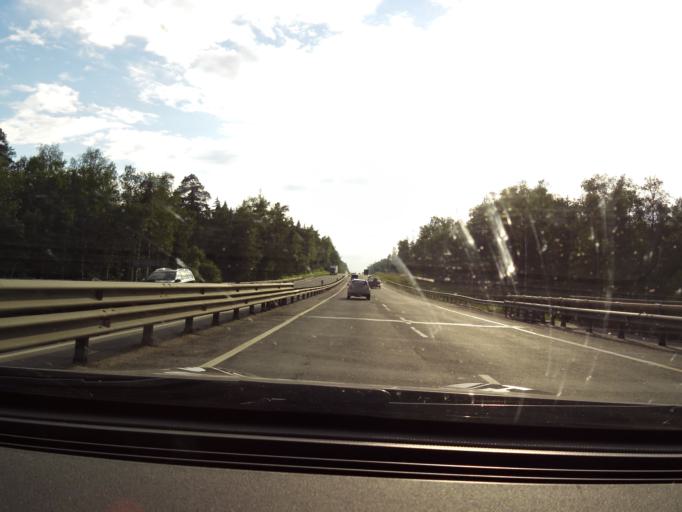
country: RU
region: Vladimir
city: Novki
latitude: 56.2005
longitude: 41.0770
